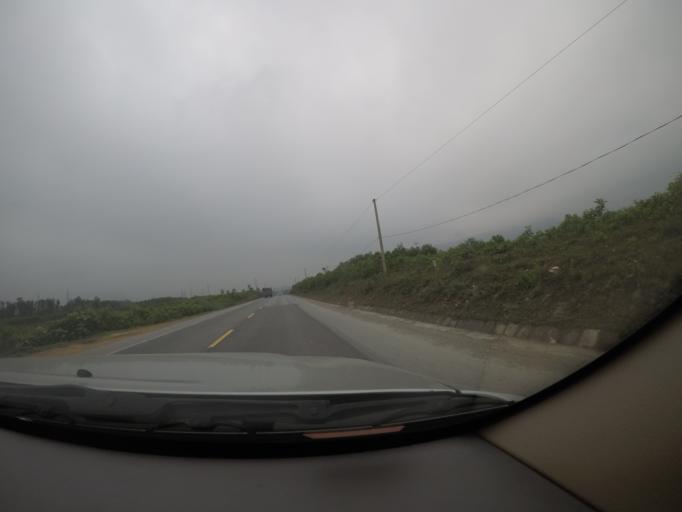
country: VN
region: Ha Tinh
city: Ky Anh
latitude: 18.0346
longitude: 106.3122
